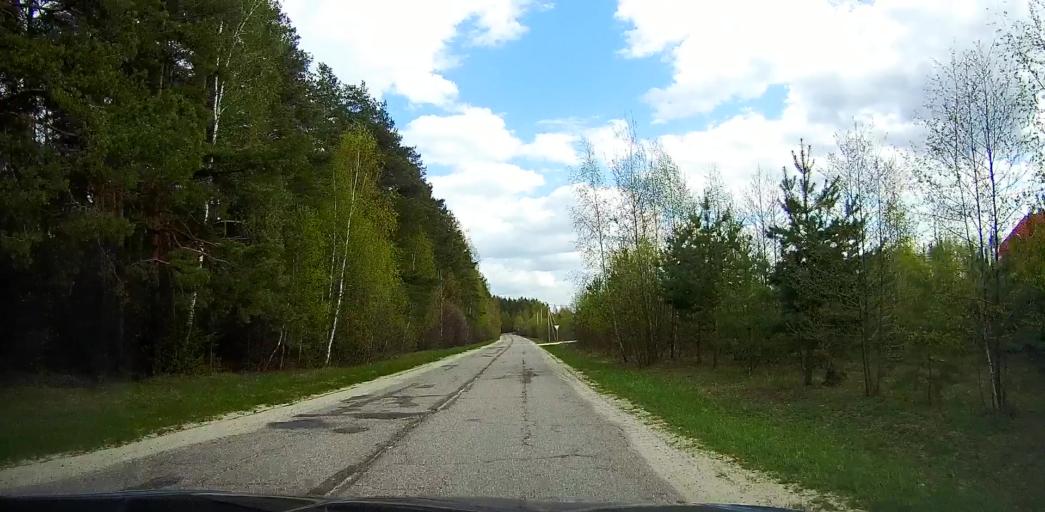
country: RU
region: Moskovskaya
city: Davydovo
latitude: 55.6461
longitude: 38.7688
